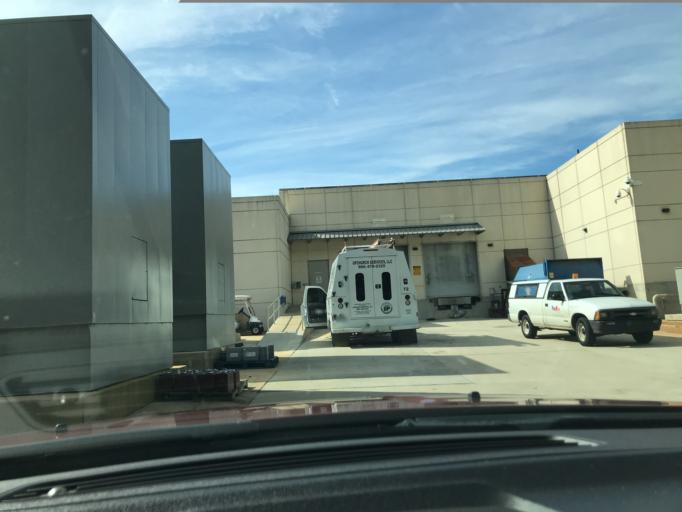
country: US
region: Tennessee
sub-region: Shelby County
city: Collierville
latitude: 35.0354
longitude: -89.7202
